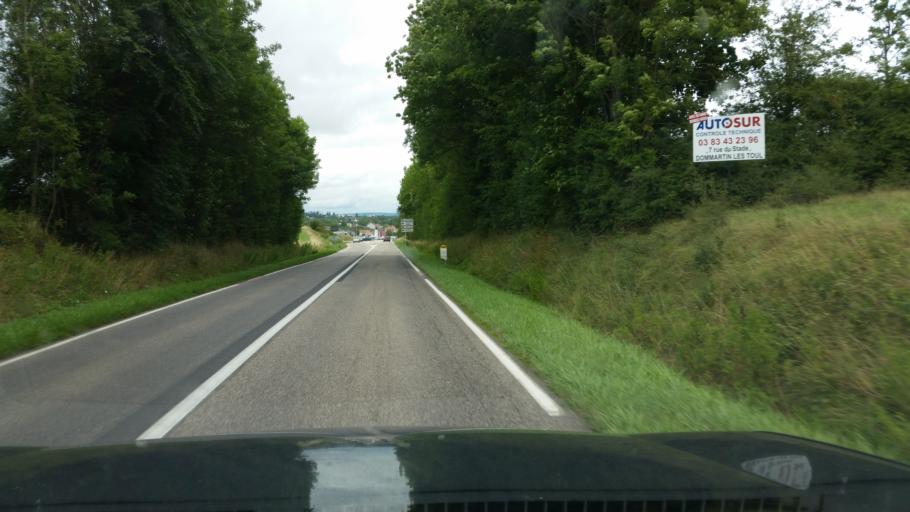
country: FR
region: Lorraine
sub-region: Departement de Meurthe-et-Moselle
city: Toul
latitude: 48.6592
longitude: 5.8764
